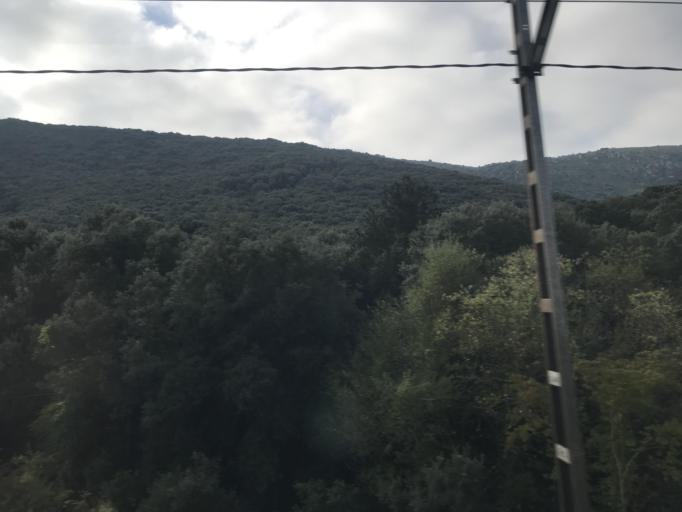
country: ES
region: Castille and Leon
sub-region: Provincia de Burgos
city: Ameyugo
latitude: 42.6484
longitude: -3.0712
